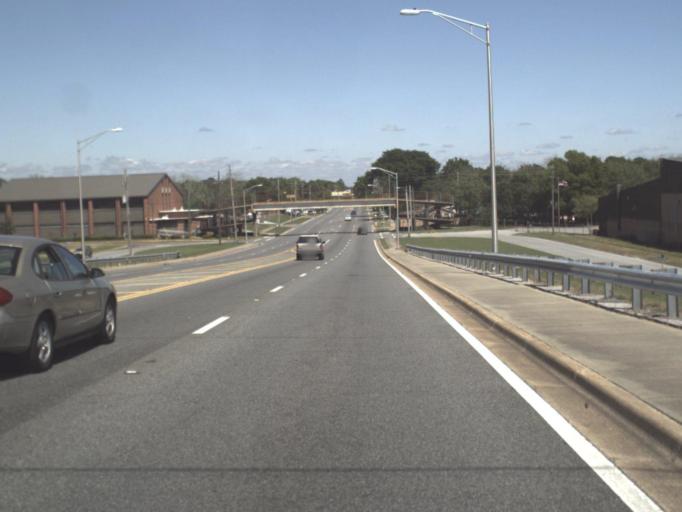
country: US
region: Florida
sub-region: Escambia County
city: Goulding
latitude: 30.4458
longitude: -87.2235
